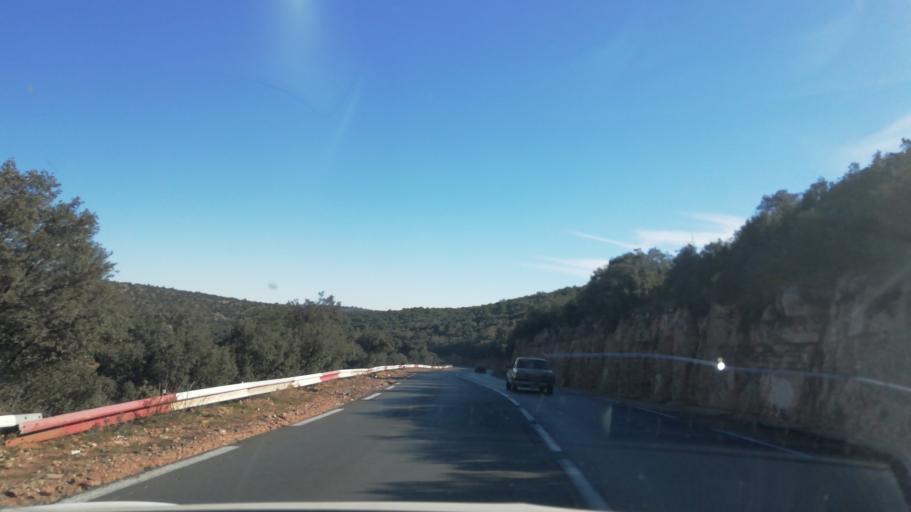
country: DZ
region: Tlemcen
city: Sebdou
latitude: 34.7416
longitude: -1.3471
